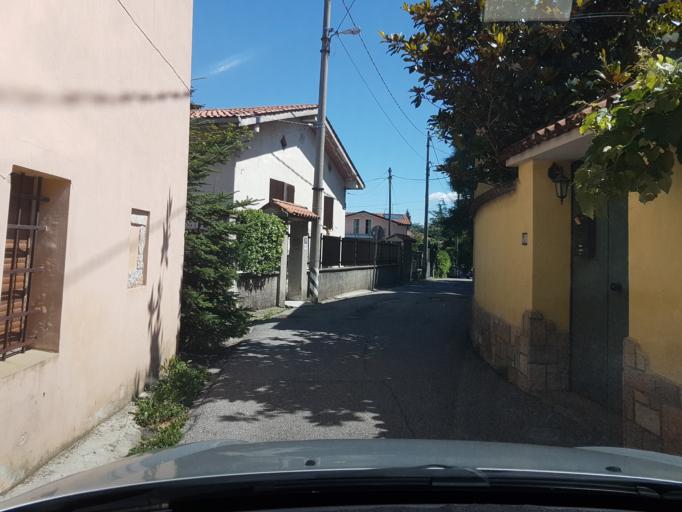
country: IT
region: Friuli Venezia Giulia
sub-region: Provincia di Trieste
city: Villa Opicina
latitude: 45.6904
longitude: 13.7892
